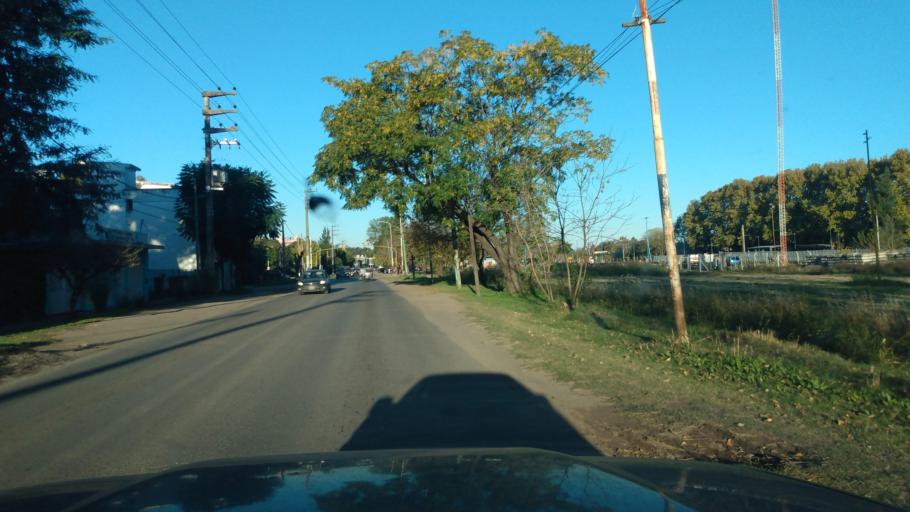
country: AR
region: Buenos Aires
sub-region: Partido de General Rodriguez
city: General Rodriguez
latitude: -34.6310
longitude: -58.8562
